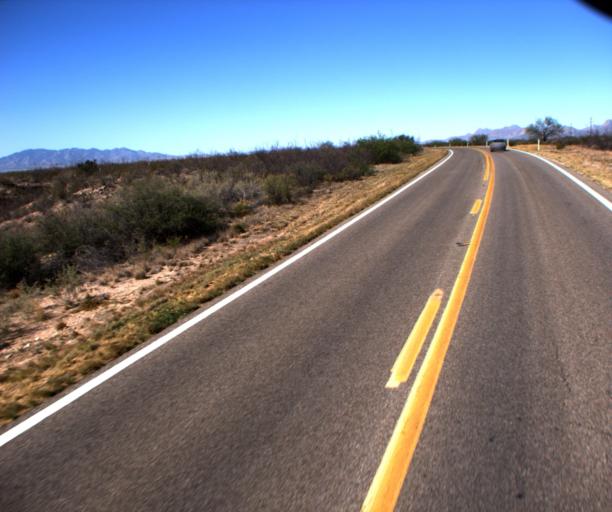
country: US
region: Arizona
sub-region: Cochise County
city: Huachuca City
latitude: 31.7195
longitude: -110.2393
